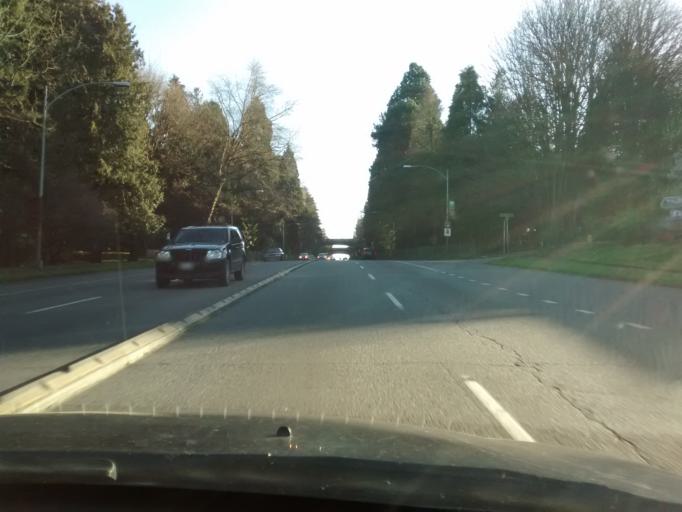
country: US
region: Washington
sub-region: King County
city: Seattle
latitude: 47.6722
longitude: -122.3473
